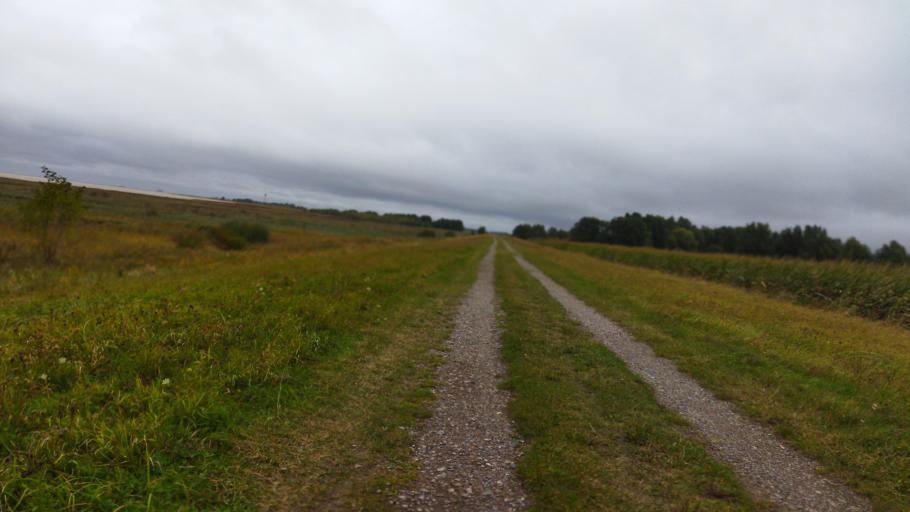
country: NL
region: Groningen
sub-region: Gemeente Delfzijl
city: Delfzijl
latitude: 53.3702
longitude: 7.0080
